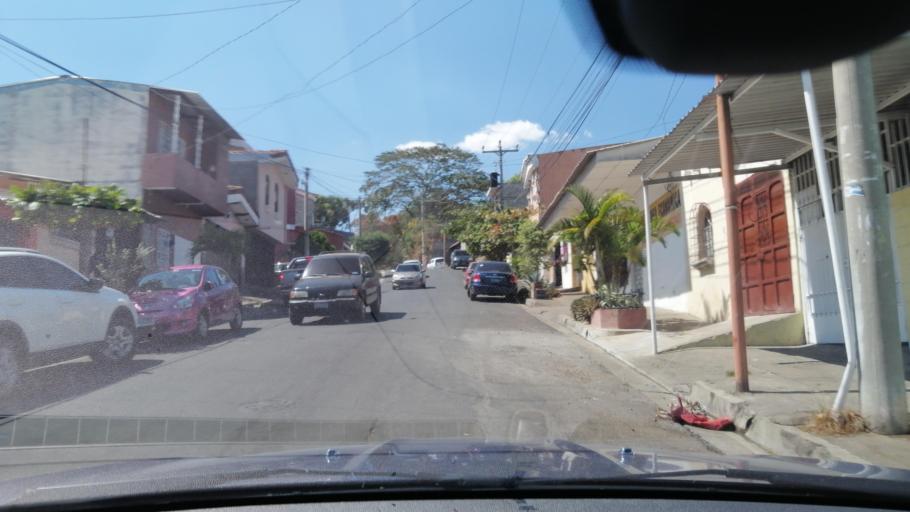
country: SV
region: Santa Ana
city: Santa Ana
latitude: 13.9620
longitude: -89.5714
